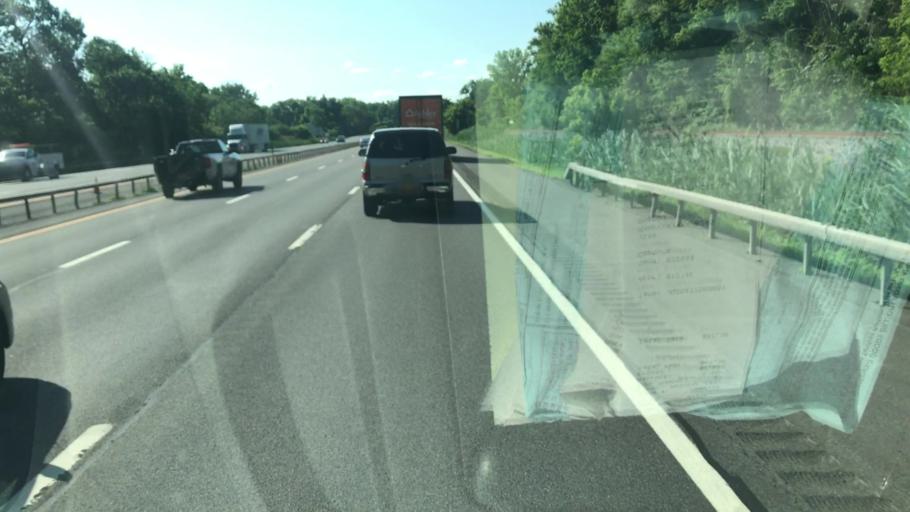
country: US
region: New York
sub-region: Onondaga County
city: Lakeland
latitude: 43.0968
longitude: -76.2392
